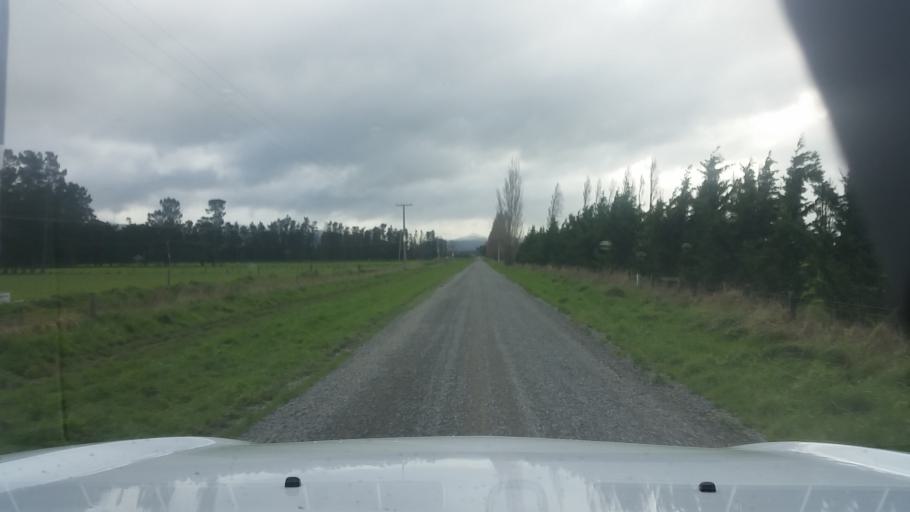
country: NZ
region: Wellington
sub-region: South Wairarapa District
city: Waipawa
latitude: -41.1657
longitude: 175.4201
